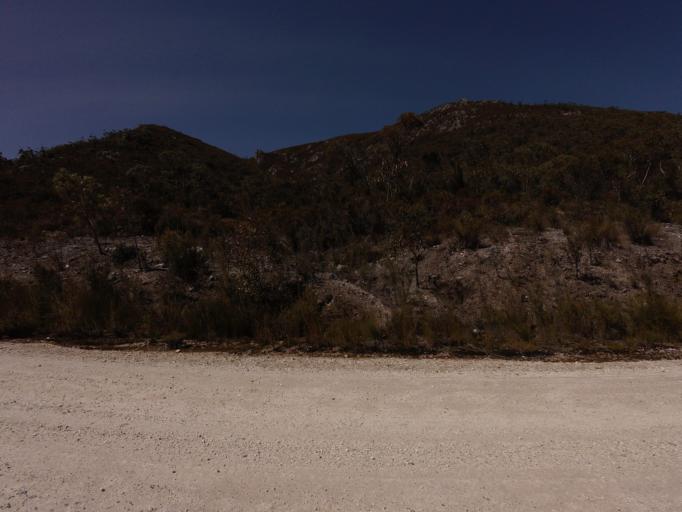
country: AU
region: Tasmania
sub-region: Huon Valley
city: Geeveston
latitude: -42.9261
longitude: 146.3461
